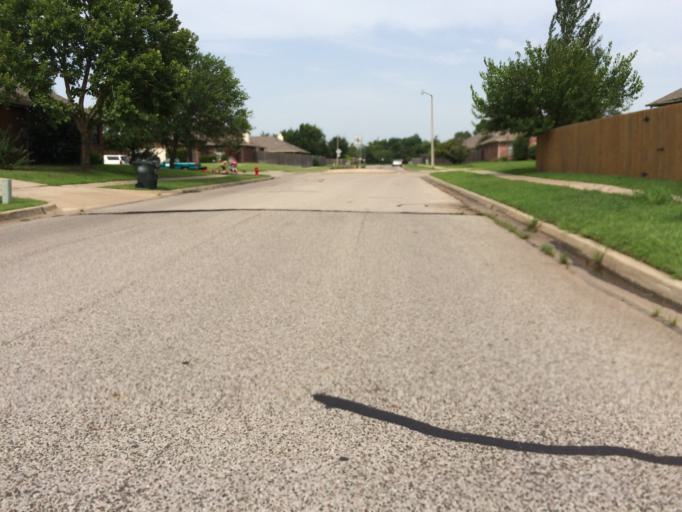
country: US
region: Oklahoma
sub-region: Cleveland County
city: Norman
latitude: 35.1987
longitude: -97.4204
